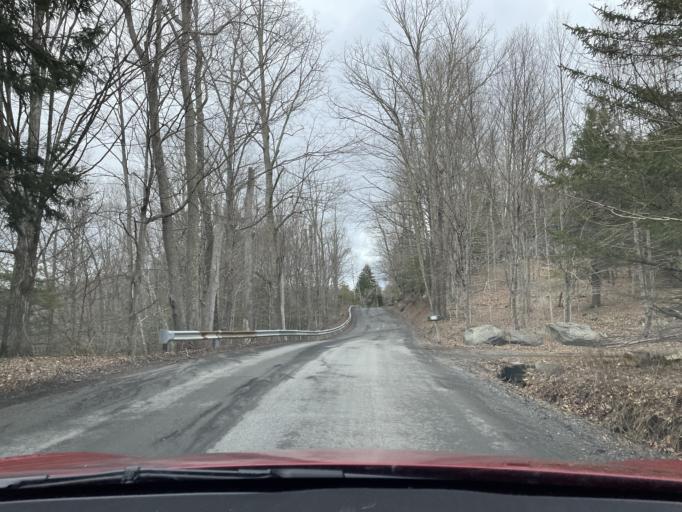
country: US
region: New York
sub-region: Ulster County
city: Woodstock
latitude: 42.0712
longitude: -74.1553
